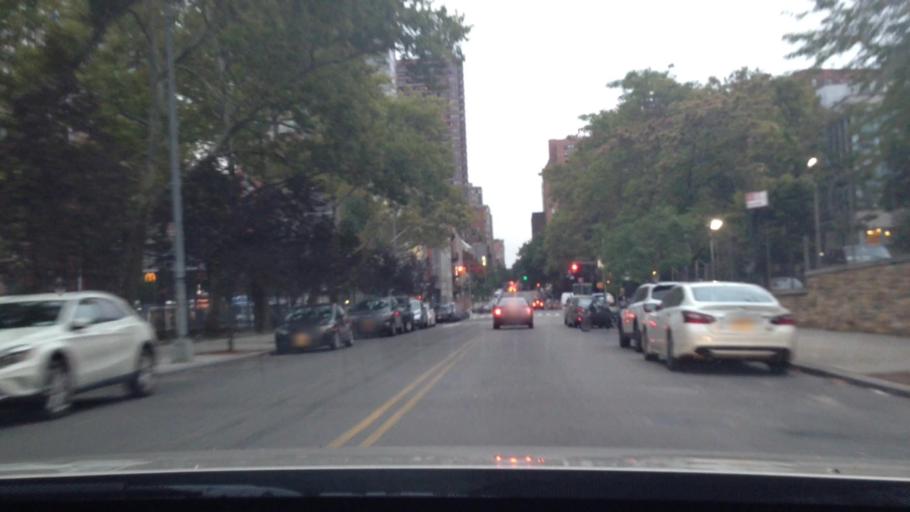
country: US
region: New York
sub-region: New York County
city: Manhattan
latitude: 40.7844
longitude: -73.9454
